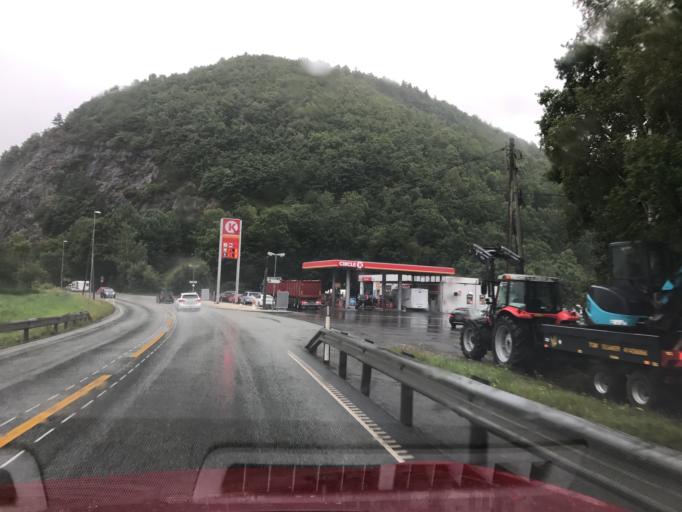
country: NO
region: Rogaland
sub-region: Lund
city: Moi
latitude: 58.4052
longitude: 6.6227
